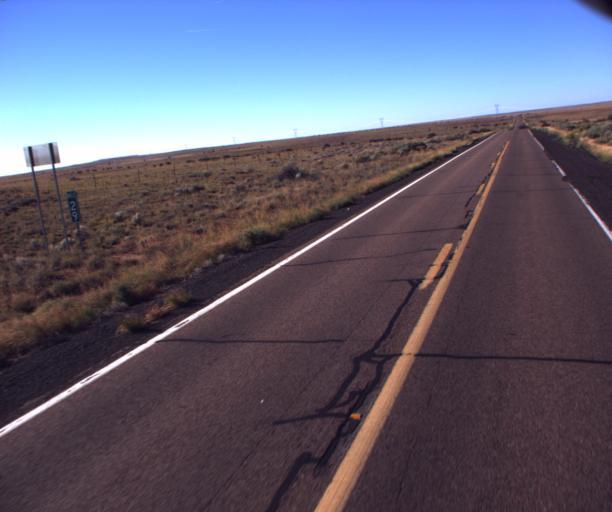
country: US
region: Arizona
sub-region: Navajo County
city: Holbrook
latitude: 34.8085
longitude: -110.2043
